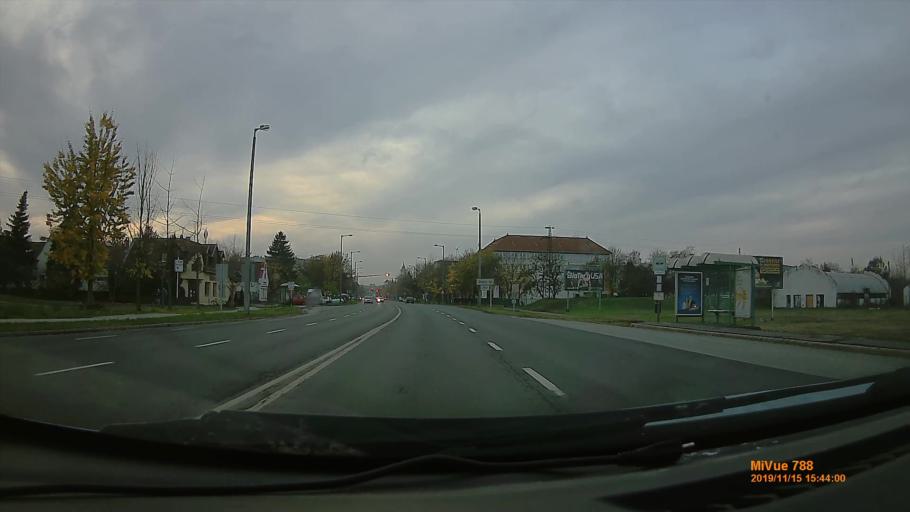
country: HU
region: Bekes
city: Bekescsaba
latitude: 46.6818
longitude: 21.1115
